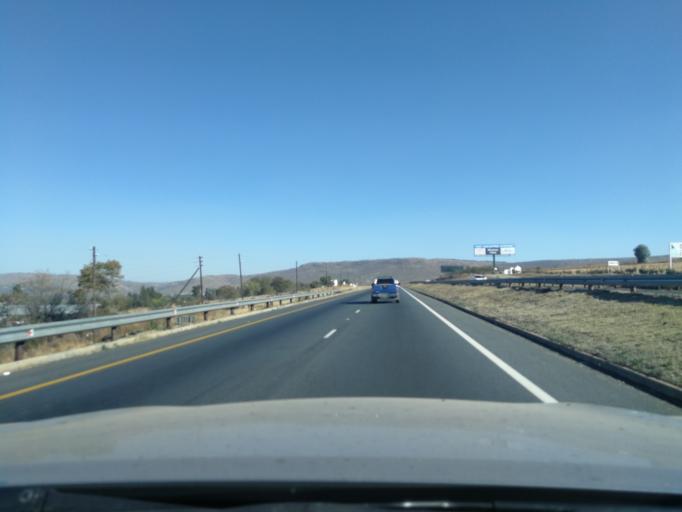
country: ZA
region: Gauteng
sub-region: West Rand District Municipality
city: Muldersdriseloop
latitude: -26.0506
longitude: 27.8390
